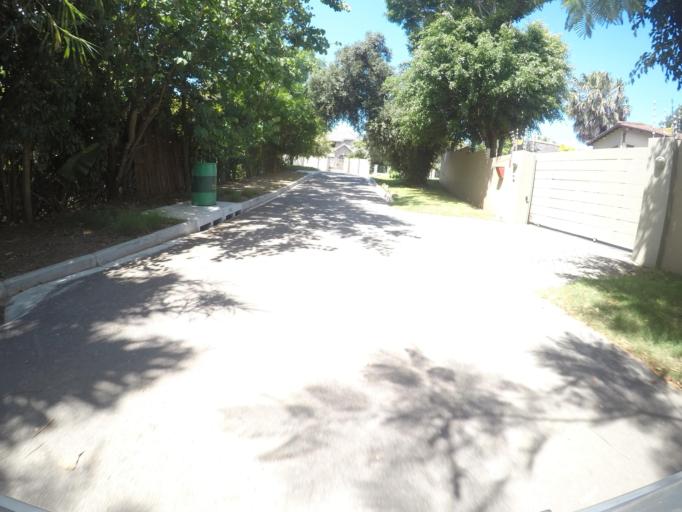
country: ZA
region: Eastern Cape
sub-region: Buffalo City Metropolitan Municipality
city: East London
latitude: -32.9736
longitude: 27.9052
